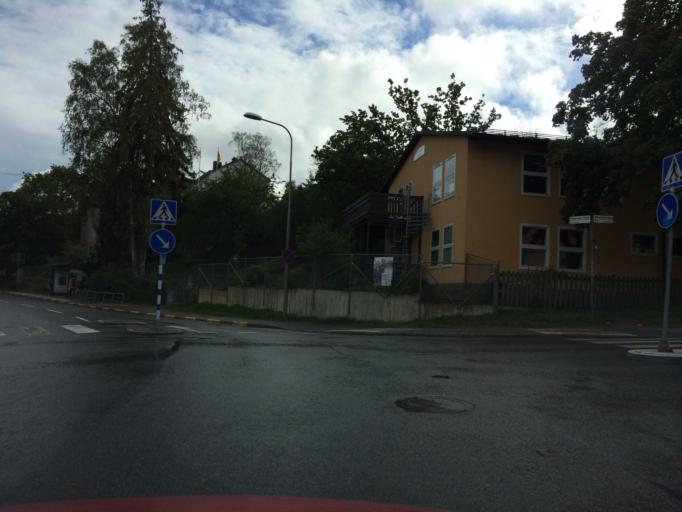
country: SE
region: Stockholm
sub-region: Huddinge Kommun
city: Segeltorp
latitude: 59.3016
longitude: 17.9562
